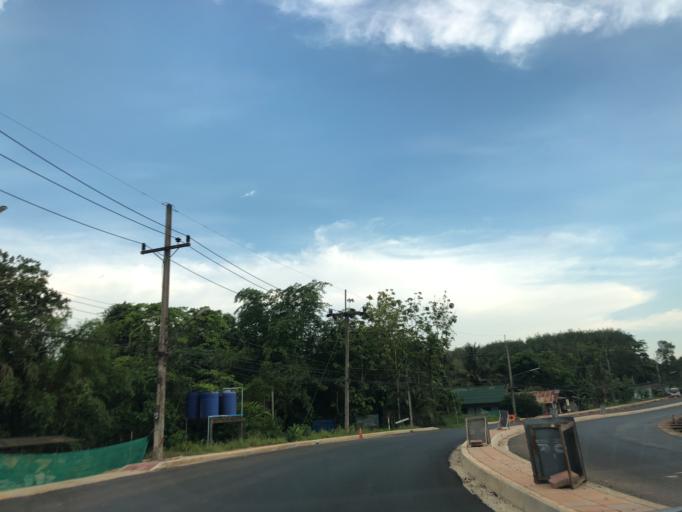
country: TH
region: Phangnga
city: Ban Ao Nang
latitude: 8.0661
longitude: 98.8438
